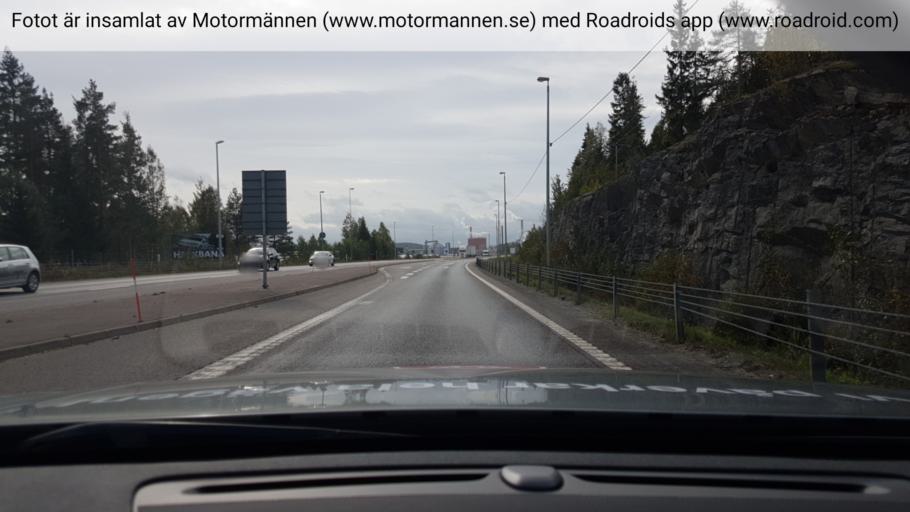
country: SE
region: Vaermland
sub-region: Grums Kommun
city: Grums
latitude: 59.3552
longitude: 13.1310
